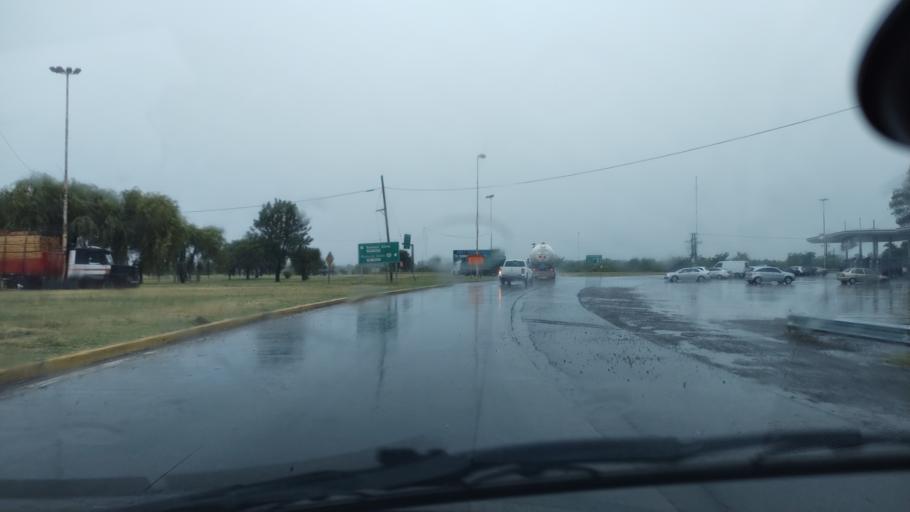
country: AR
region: Buenos Aires
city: Canuelas
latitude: -35.0269
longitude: -58.7455
